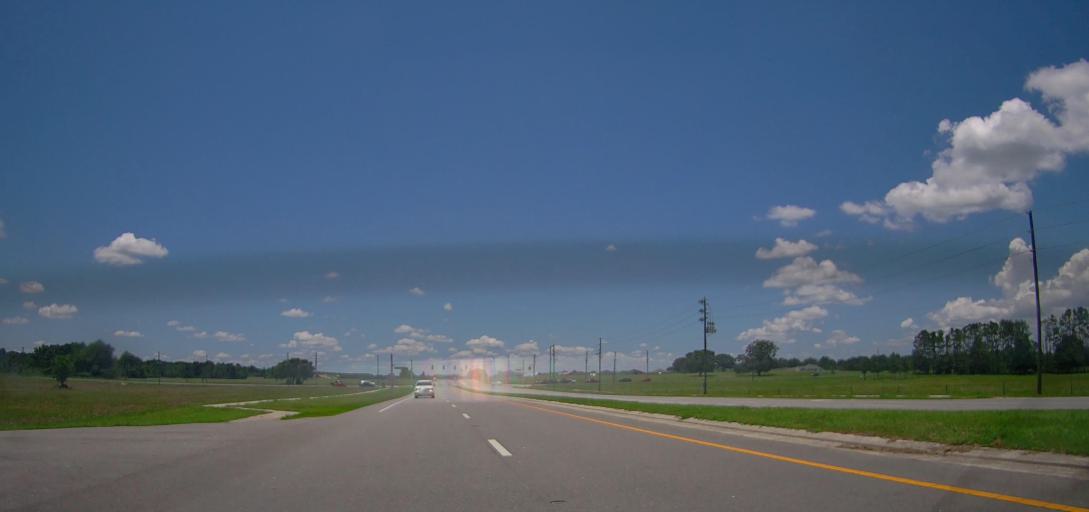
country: US
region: Florida
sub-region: Marion County
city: Belleview
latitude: 29.0862
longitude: -82.0511
